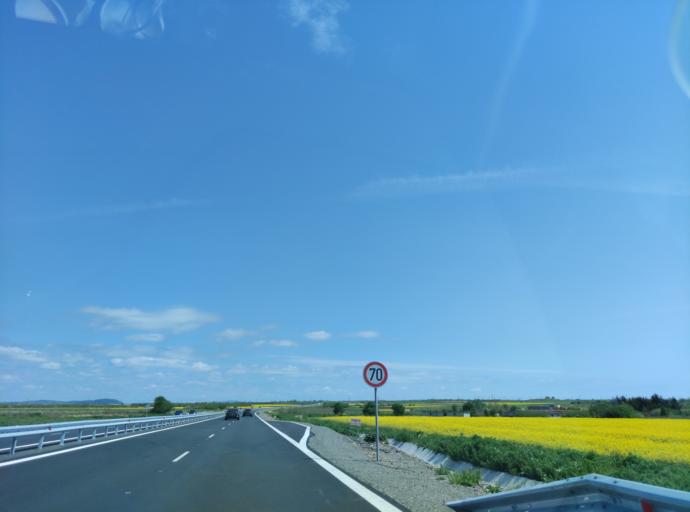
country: BG
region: Burgas
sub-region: Obshtina Pomorie
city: Pomorie
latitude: 42.5689
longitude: 27.5733
